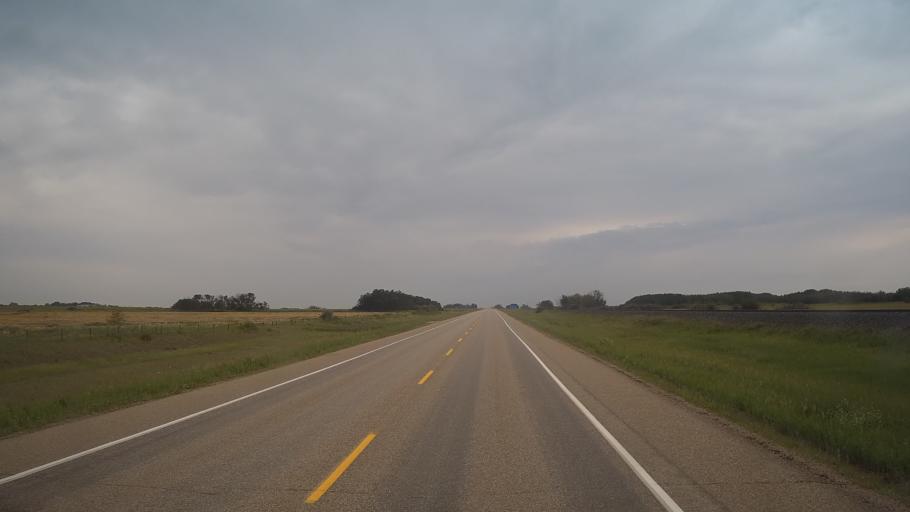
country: CA
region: Saskatchewan
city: Langham
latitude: 52.1269
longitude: -107.2705
